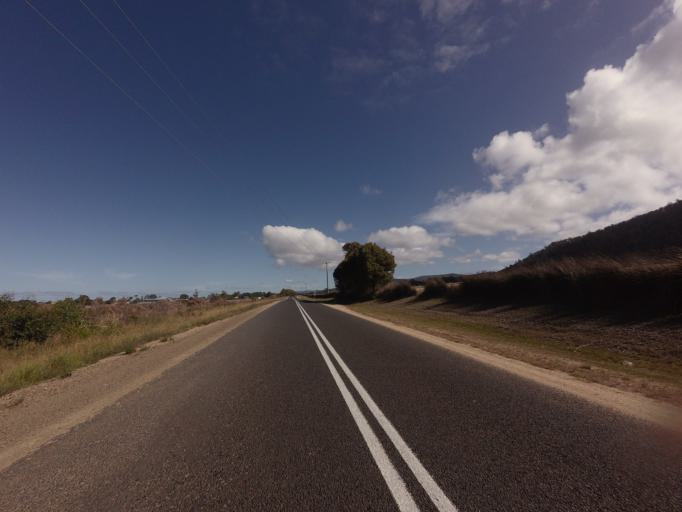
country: AU
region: Tasmania
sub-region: Break O'Day
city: St Helens
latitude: -41.7373
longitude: 148.2748
